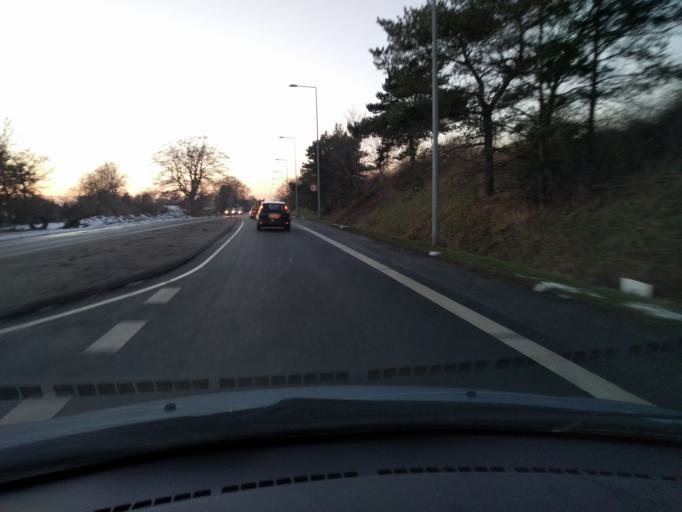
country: DK
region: South Denmark
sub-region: Nyborg Kommune
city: Ullerslev
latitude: 55.3617
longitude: 10.6794
